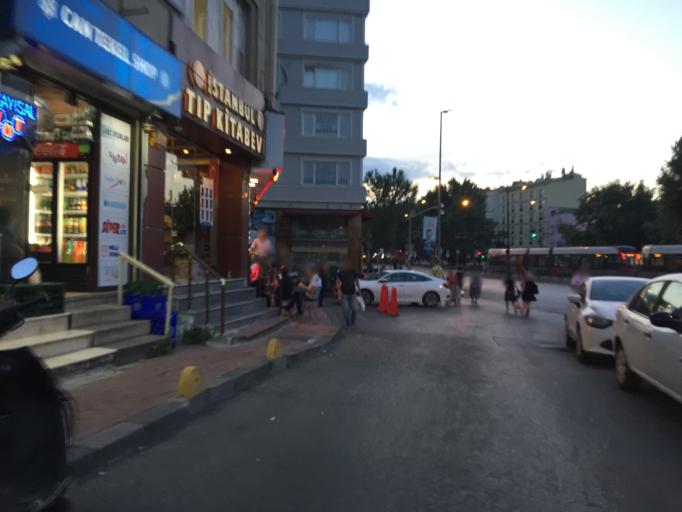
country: TR
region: Istanbul
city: Istanbul
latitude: 41.0156
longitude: 28.9319
